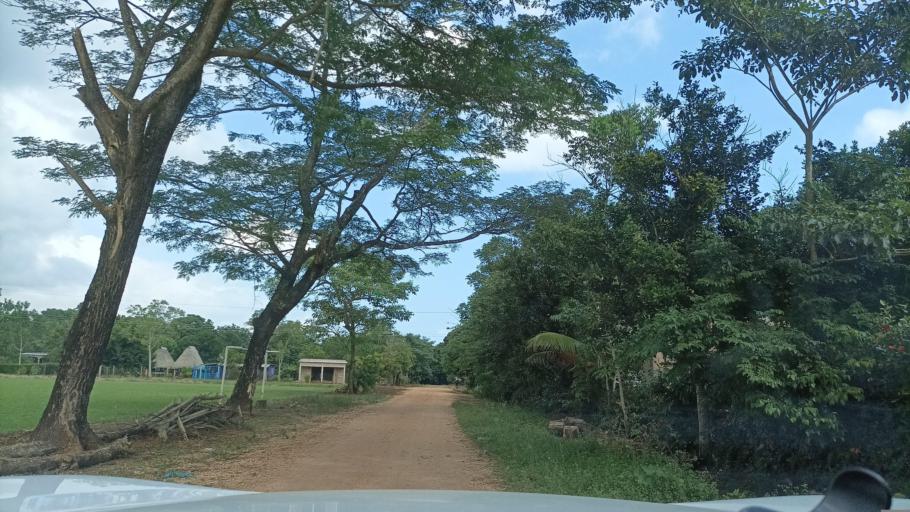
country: MX
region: Veracruz
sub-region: Pajapan
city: Pajapan
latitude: 18.1840
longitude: -94.6717
